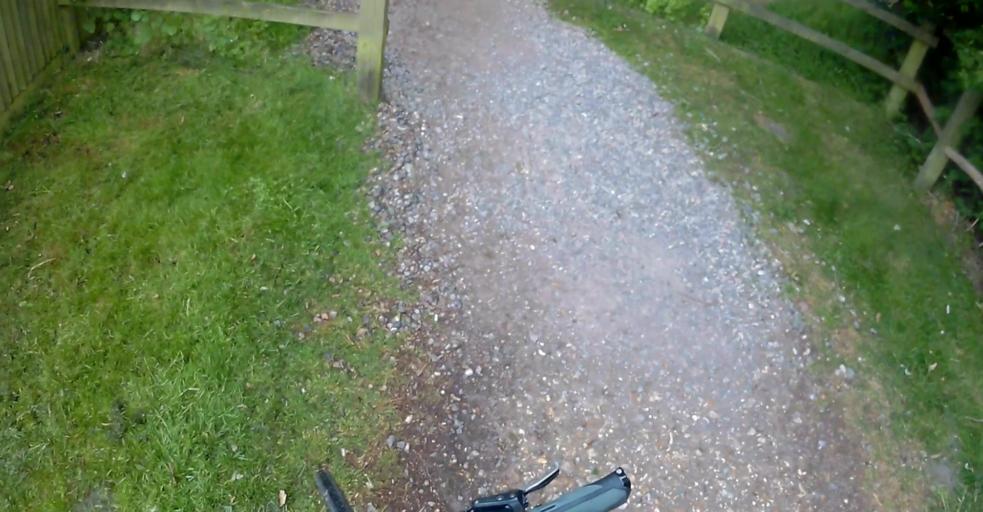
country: GB
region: England
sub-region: Hampshire
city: Farnborough
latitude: 51.2882
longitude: -0.7881
